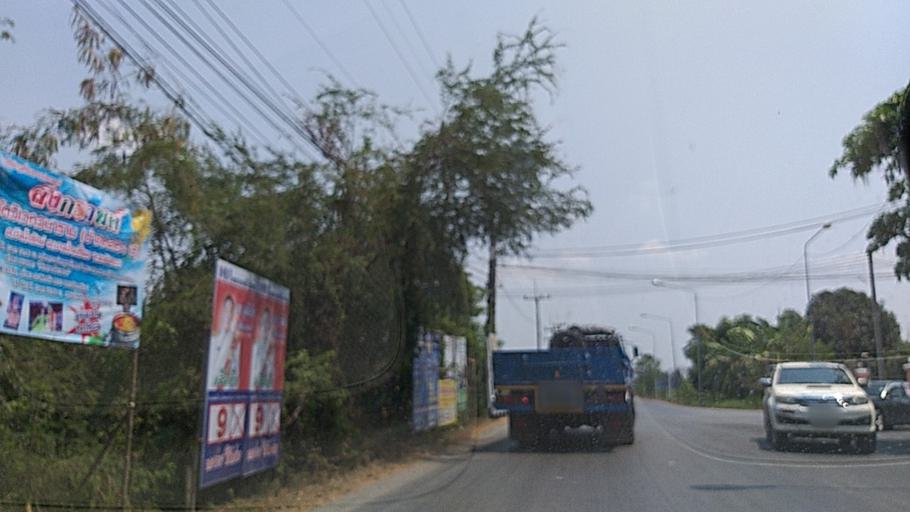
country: TH
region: Chachoengsao
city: Bang Nam Priao
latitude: 13.9717
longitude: 100.9660
